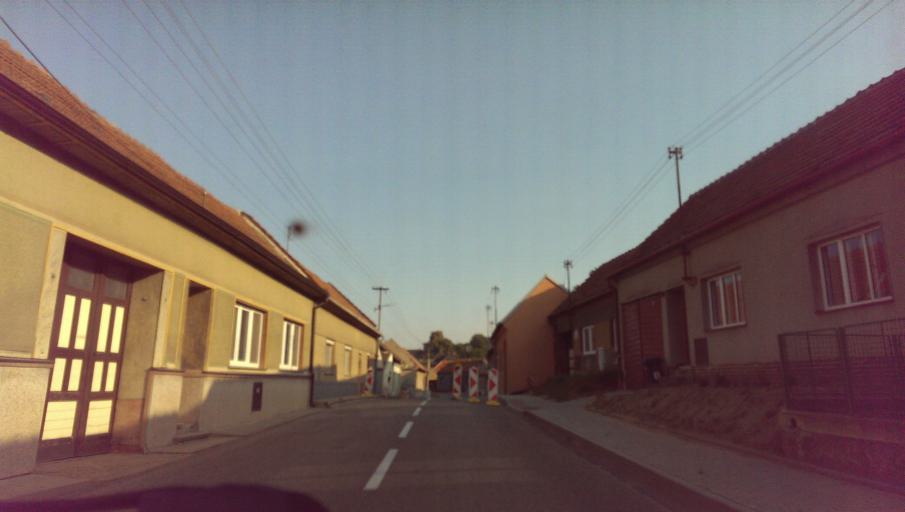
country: CZ
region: Zlin
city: Korycany
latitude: 49.1268
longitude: 17.1272
